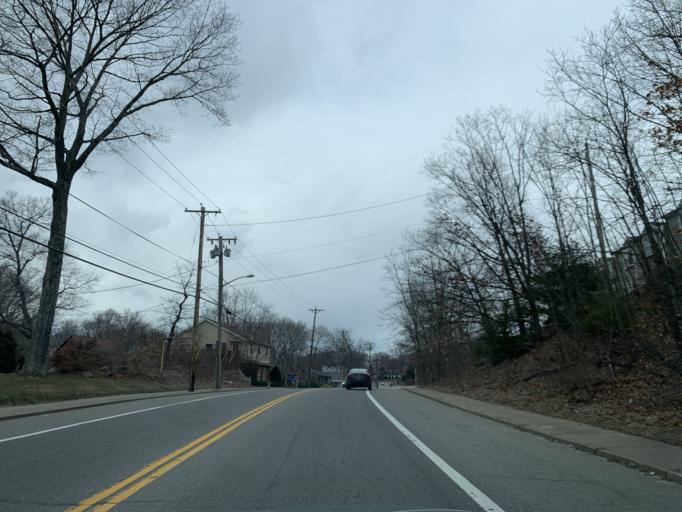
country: US
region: Rhode Island
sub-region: Providence County
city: Woonsocket
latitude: 42.0135
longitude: -71.4799
